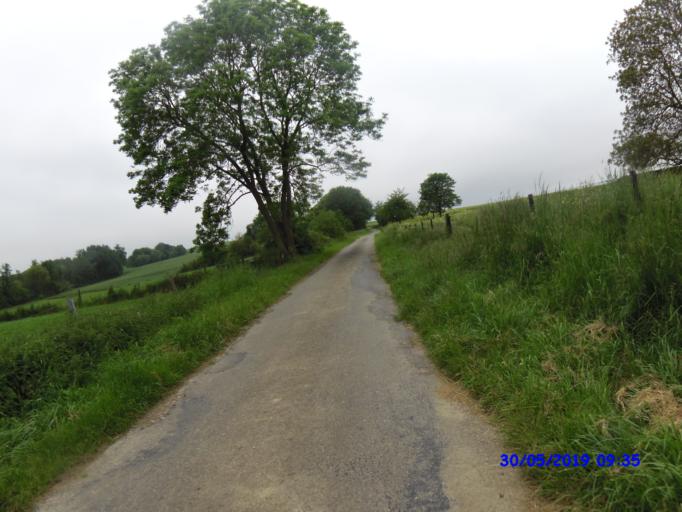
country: BE
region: Wallonia
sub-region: Province du Hainaut
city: Beaumont
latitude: 50.2527
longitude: 4.2887
